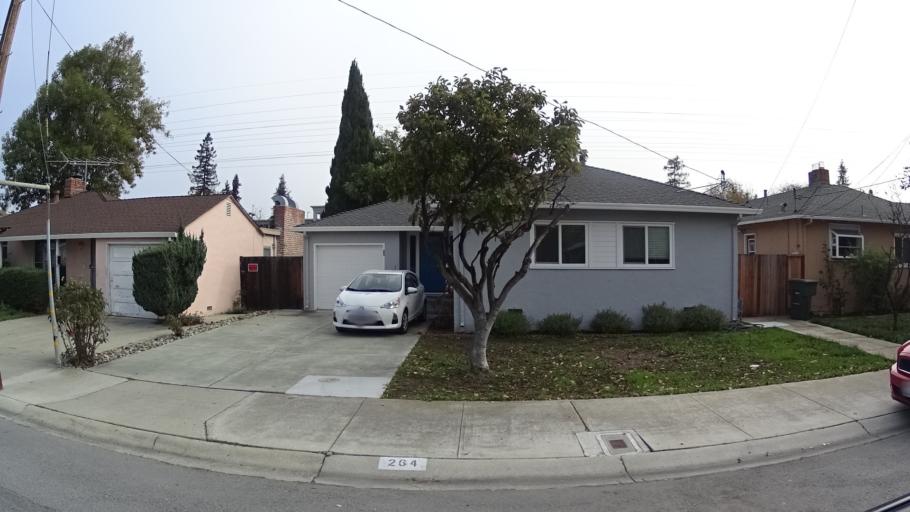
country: US
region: California
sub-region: Santa Clara County
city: Sunnyvale
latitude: 37.3770
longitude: -122.0169
